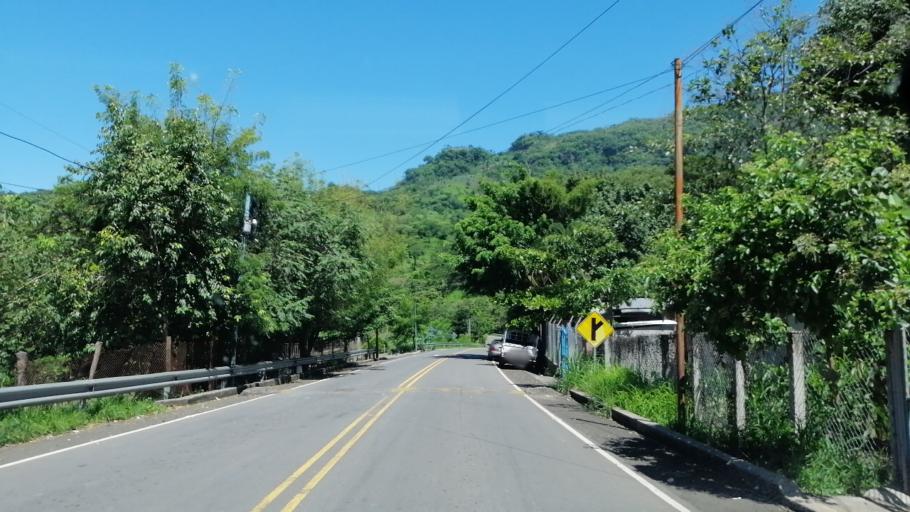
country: SV
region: San Miguel
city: Ciudad Barrios
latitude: 13.8140
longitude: -88.1843
